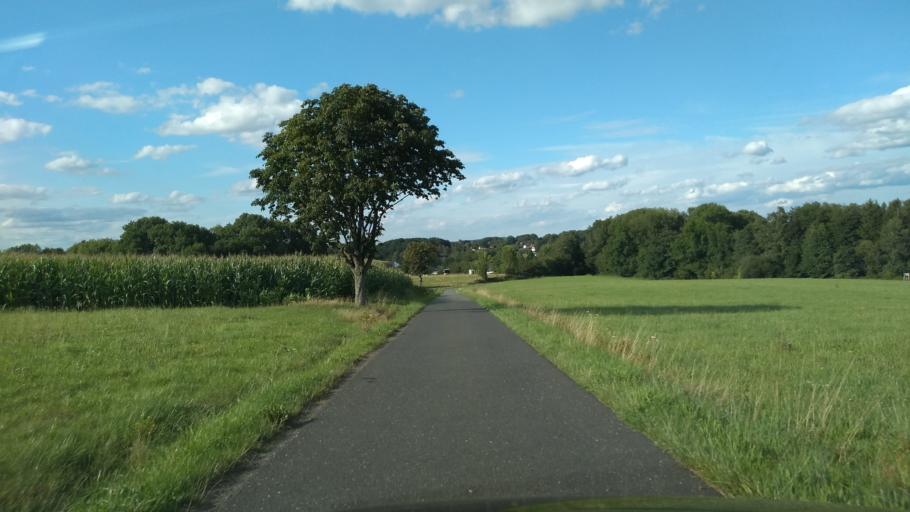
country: DE
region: North Rhine-Westphalia
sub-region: Regierungsbezirk Koln
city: Much
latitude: 50.8652
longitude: 7.3790
